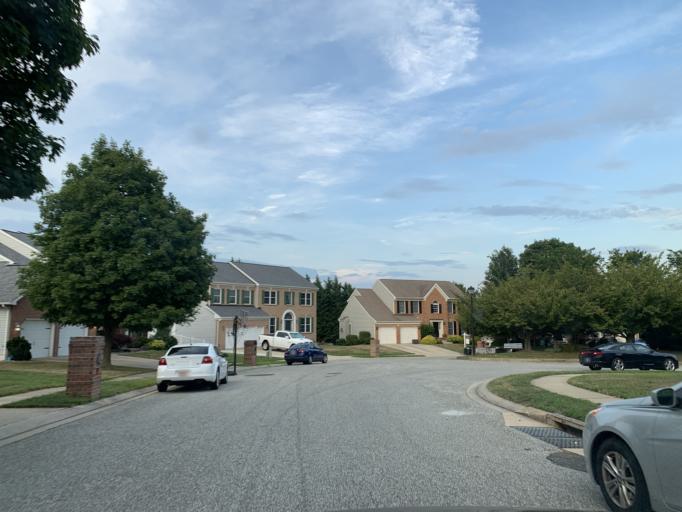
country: US
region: Maryland
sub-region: Harford County
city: Bel Air North
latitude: 39.5651
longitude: -76.3692
